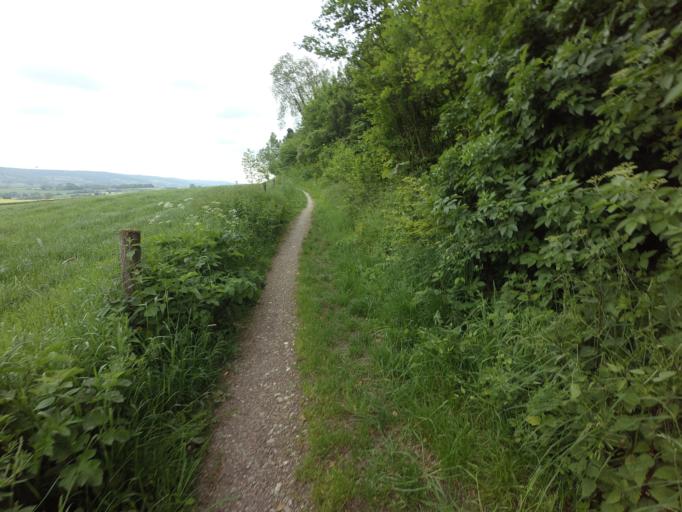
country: BE
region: Wallonia
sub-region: Province de Liege
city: Plombieres
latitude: 50.7594
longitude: 5.8962
